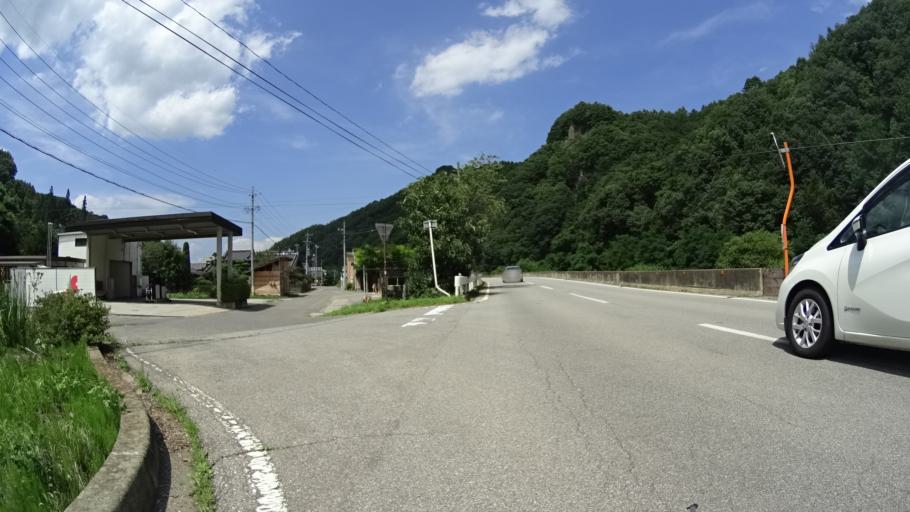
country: JP
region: Nagano
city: Saku
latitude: 36.0706
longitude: 138.4971
